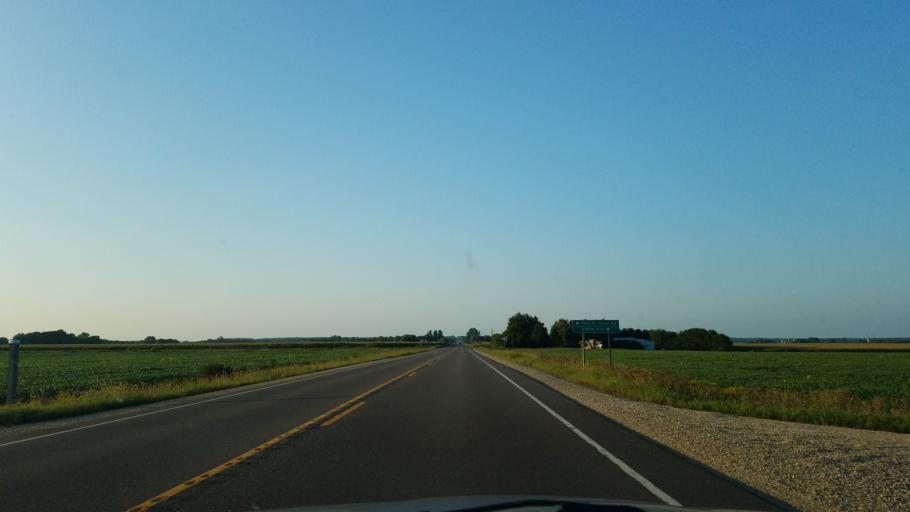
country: US
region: Wisconsin
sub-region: Polk County
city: Clear Lake
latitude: 45.2071
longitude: -92.2839
